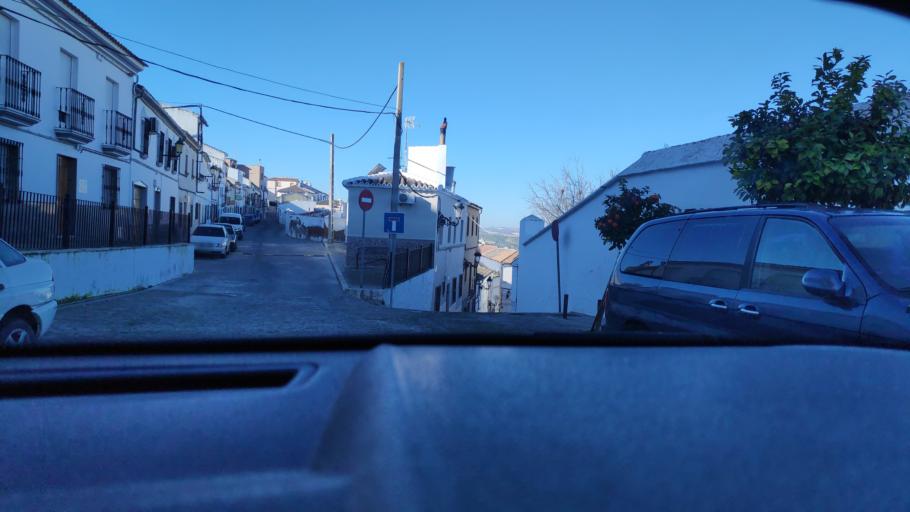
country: ES
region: Andalusia
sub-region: Province of Cordoba
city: Baena
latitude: 37.6139
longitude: -4.3270
